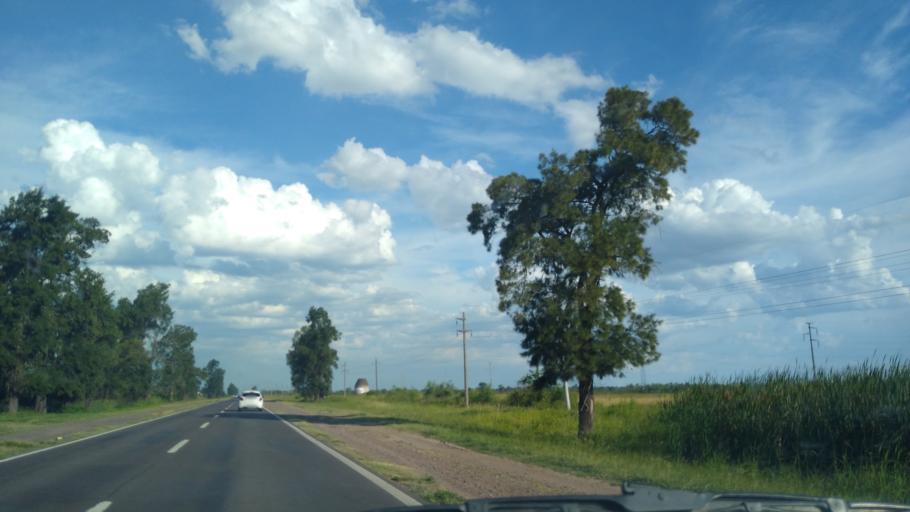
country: AR
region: Chaco
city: Presidencia Roque Saenz Pena
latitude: -26.8199
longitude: -60.3974
